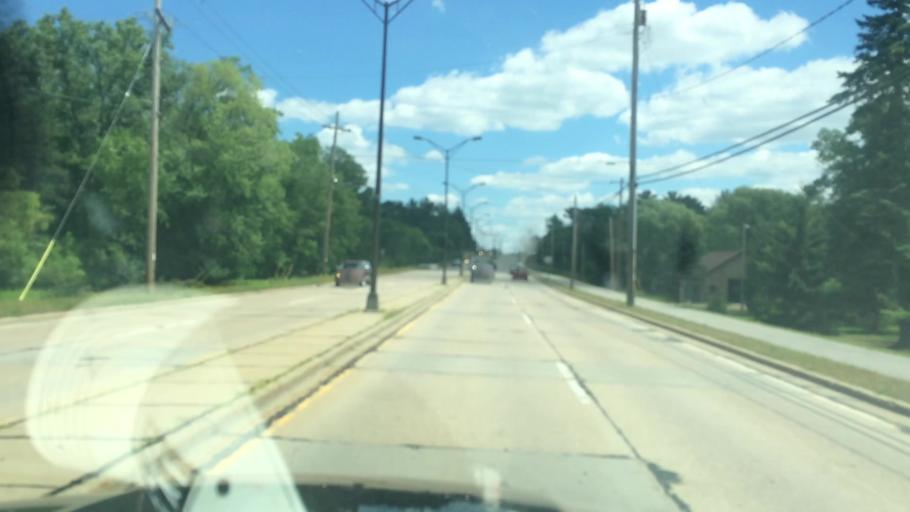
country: US
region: Wisconsin
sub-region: Portage County
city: Stevens Point
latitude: 44.5233
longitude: -89.5389
